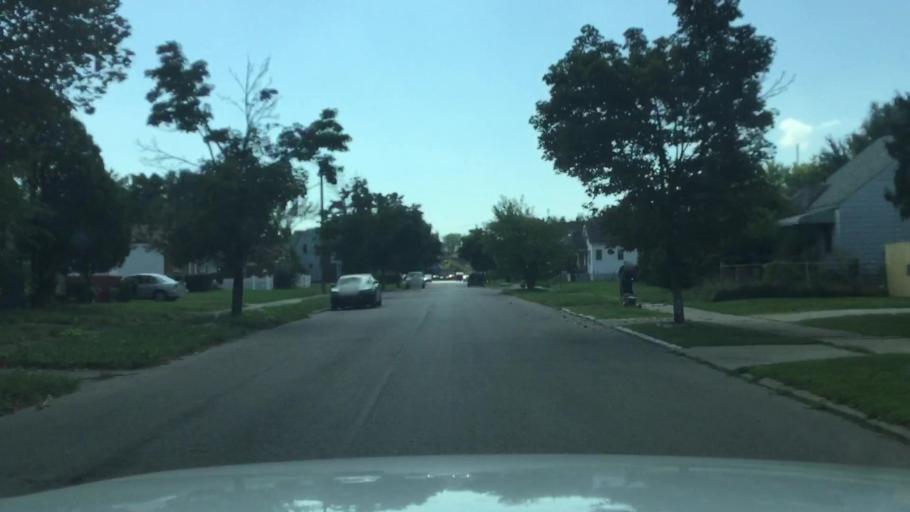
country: US
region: Michigan
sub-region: Wayne County
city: Dearborn
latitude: 42.3542
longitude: -83.1462
